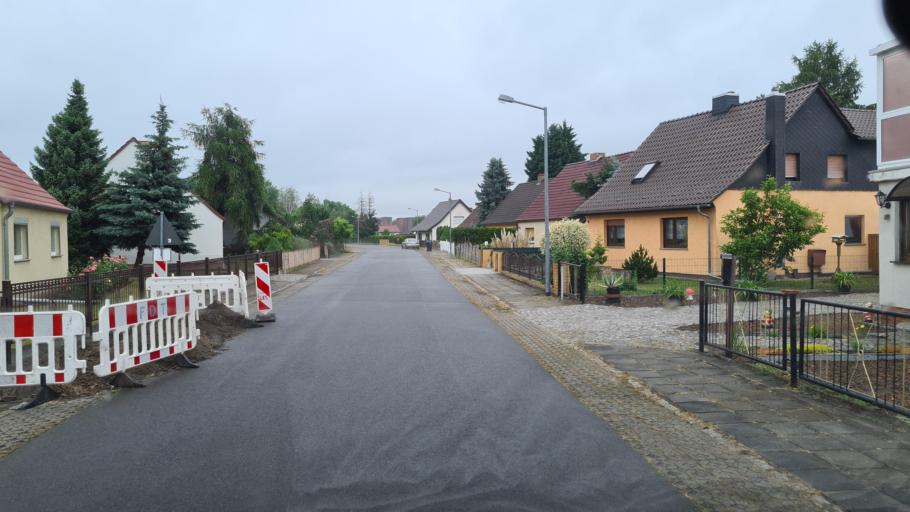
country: DE
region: Brandenburg
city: Lauchhammer
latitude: 51.4822
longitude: 13.7259
